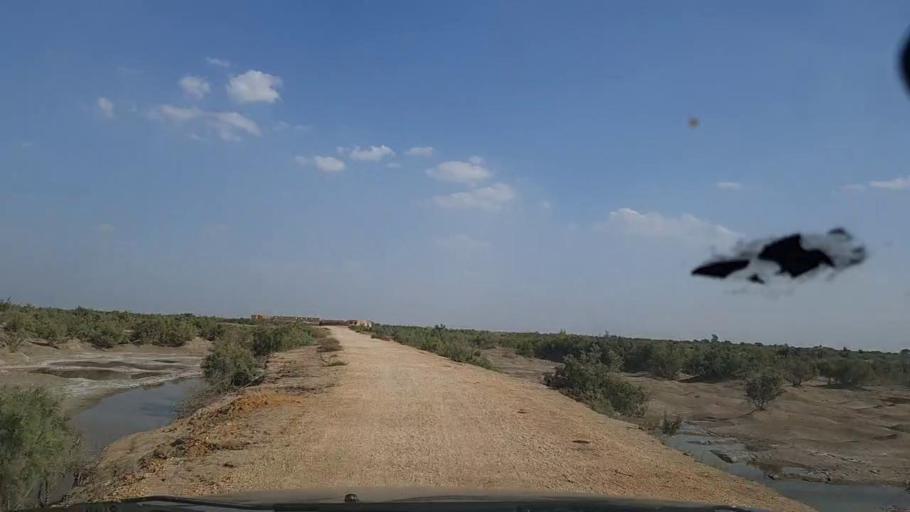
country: PK
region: Sindh
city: Daro Mehar
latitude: 24.7878
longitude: 68.0769
